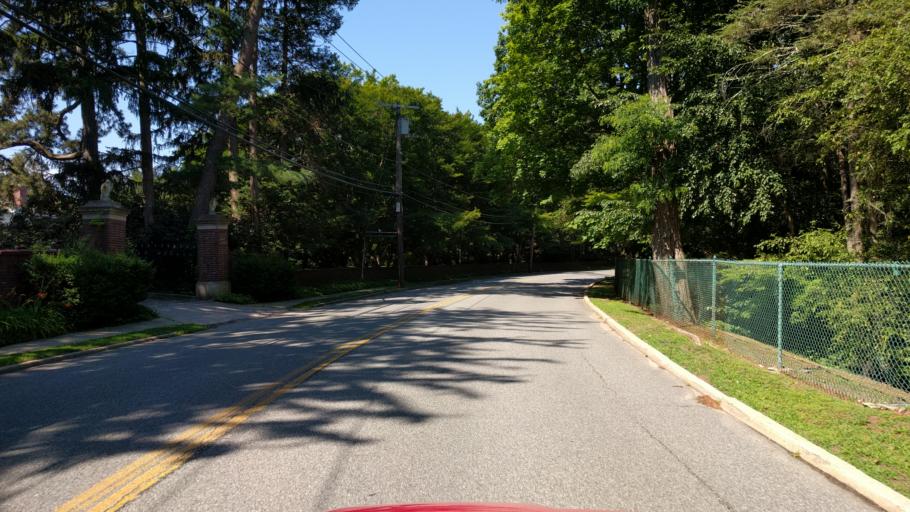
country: US
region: New York
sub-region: Nassau County
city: Locust Valley
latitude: 40.8824
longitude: -73.5886
